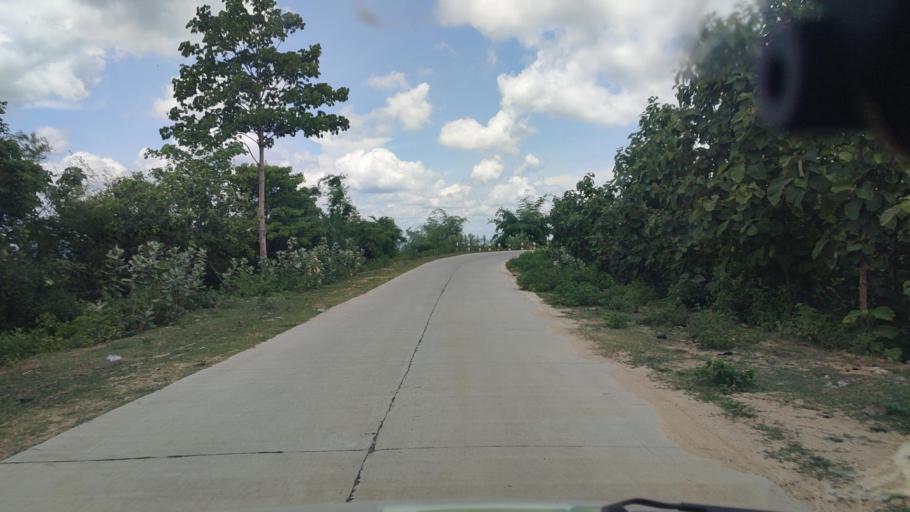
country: MM
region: Magway
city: Taungdwingyi
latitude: 20.0209
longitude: 95.8273
